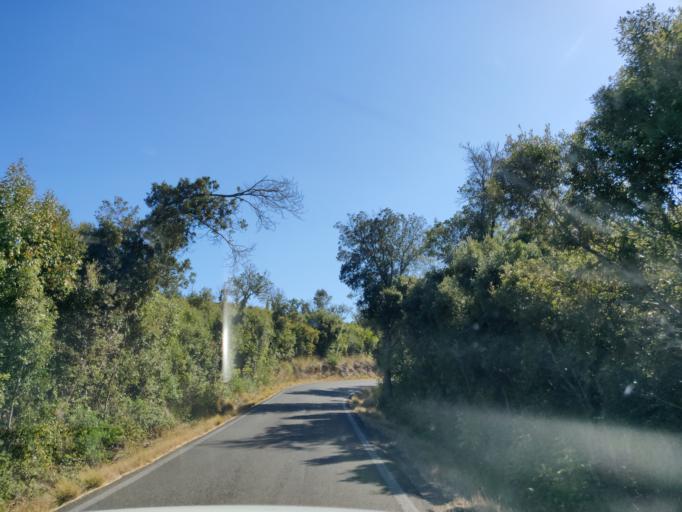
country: IT
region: Tuscany
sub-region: Provincia di Grosseto
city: Porto Ercole
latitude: 42.4243
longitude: 11.1750
